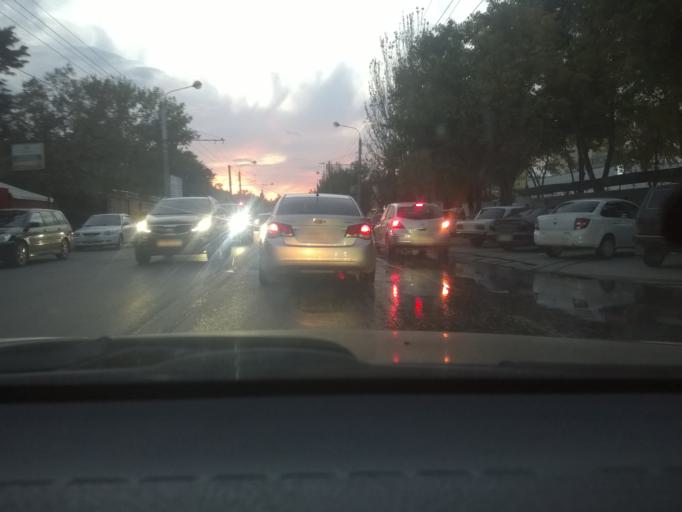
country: RU
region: Rostov
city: Rostov-na-Donu
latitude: 47.2080
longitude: 39.6311
